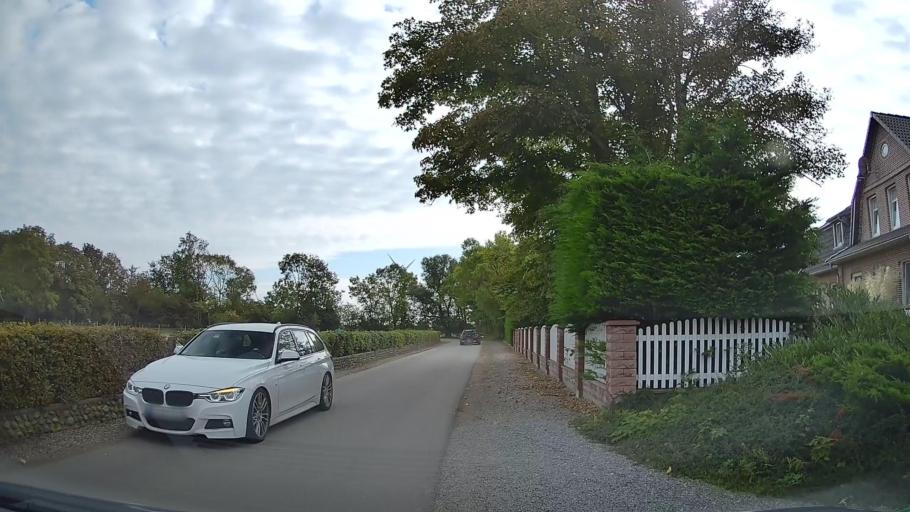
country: DE
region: Schleswig-Holstein
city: Grossenbrode
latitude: 54.5202
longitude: 11.0532
